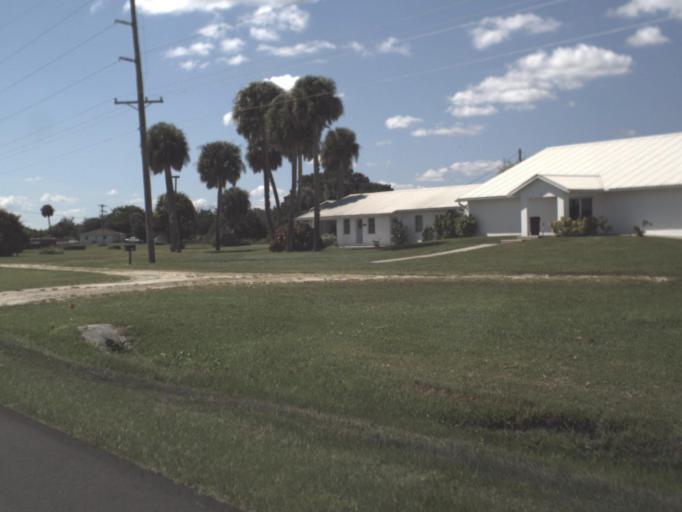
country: US
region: Florida
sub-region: Glades County
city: Moore Haven
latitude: 26.9767
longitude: -81.1129
